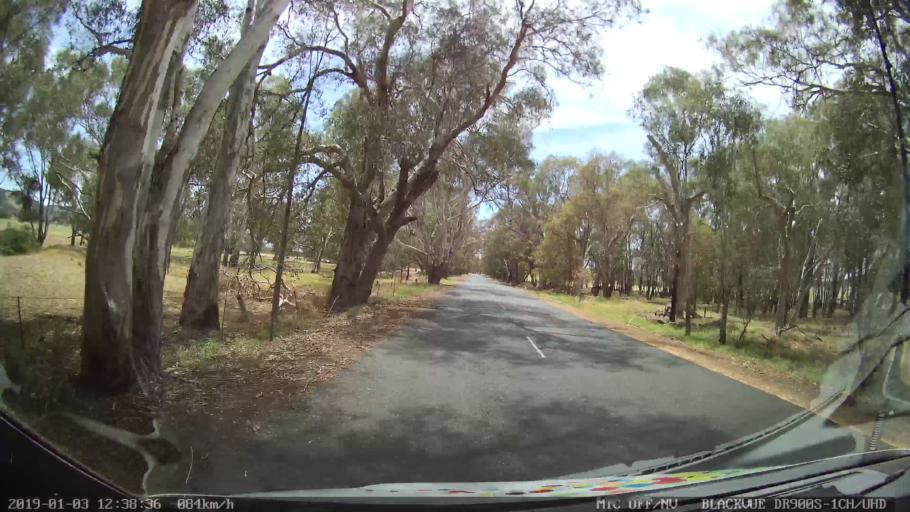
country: AU
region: New South Wales
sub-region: Weddin
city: Grenfell
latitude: -33.8321
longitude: 148.1976
